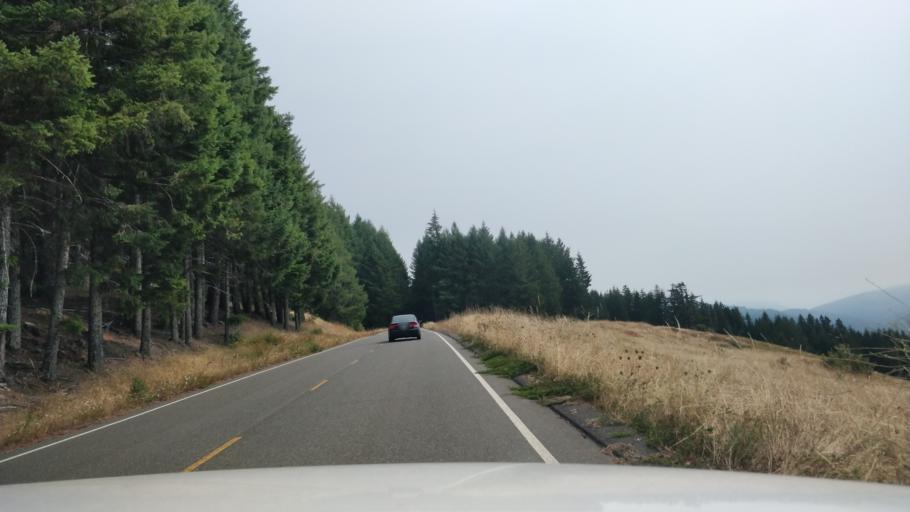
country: US
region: California
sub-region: Humboldt County
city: Westhaven-Moonstone
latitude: 41.2078
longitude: -123.9537
